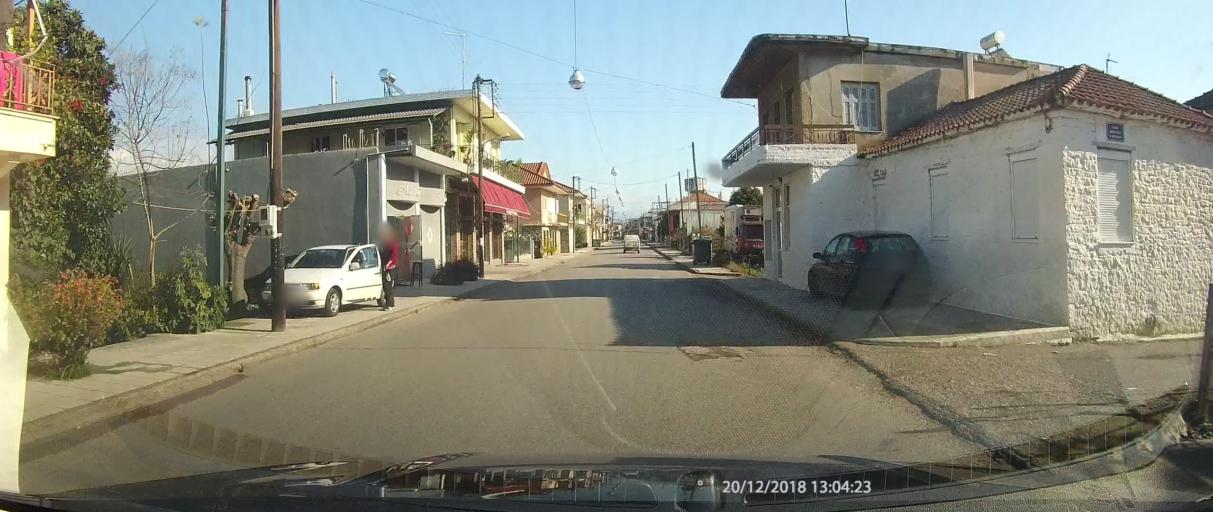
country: GR
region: West Greece
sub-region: Nomos Aitolias kai Akarnanias
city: Panaitolion
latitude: 38.5850
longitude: 21.4339
